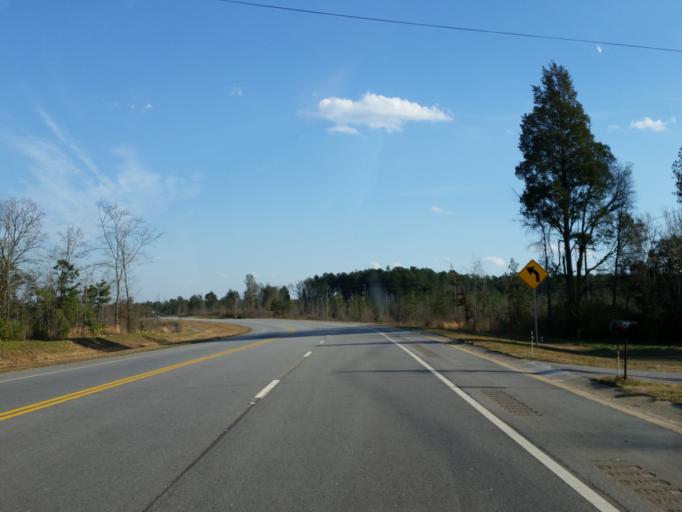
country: US
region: Georgia
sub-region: Monroe County
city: Forsyth
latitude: 33.0387
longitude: -84.0028
